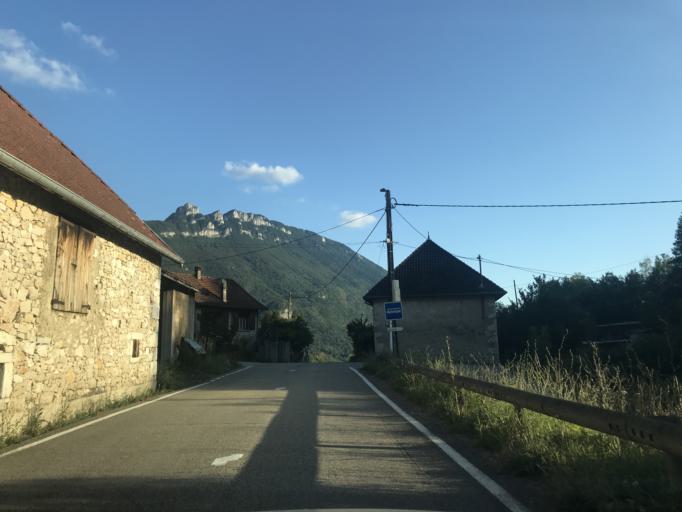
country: FR
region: Rhone-Alpes
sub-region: Departement de la Savoie
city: Brison-Saint-Innocent
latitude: 45.7095
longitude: 5.8289
